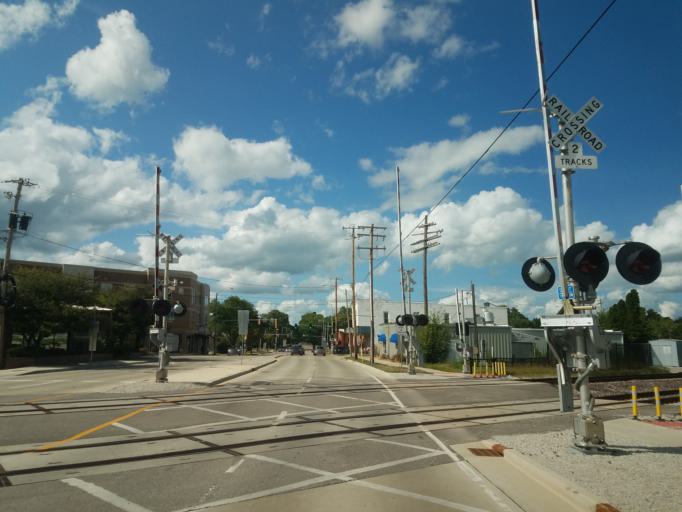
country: US
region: Illinois
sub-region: McLean County
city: Normal
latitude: 40.5095
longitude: -88.9823
